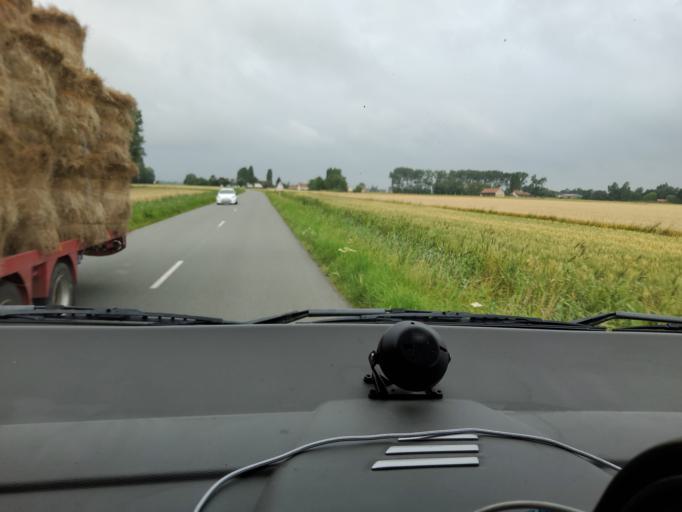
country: FR
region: Nord-Pas-de-Calais
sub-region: Departement du Pas-de-Calais
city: Sainte-Marie-Kerque
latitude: 50.9210
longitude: 2.1681
